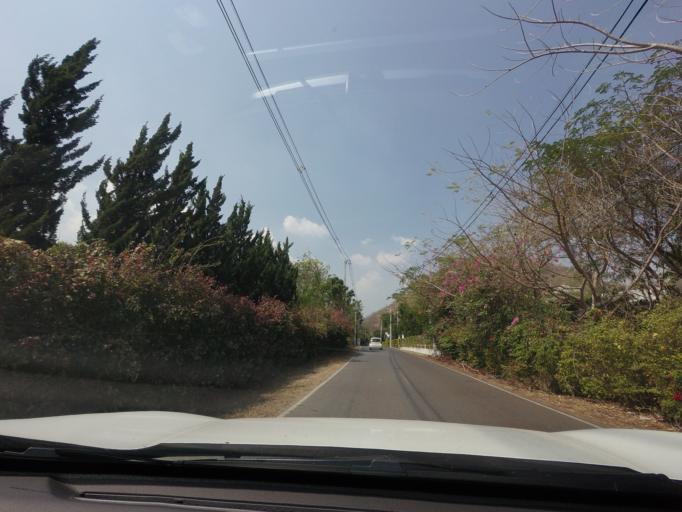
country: TH
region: Nakhon Ratchasima
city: Pak Chong
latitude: 14.5784
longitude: 101.4348
